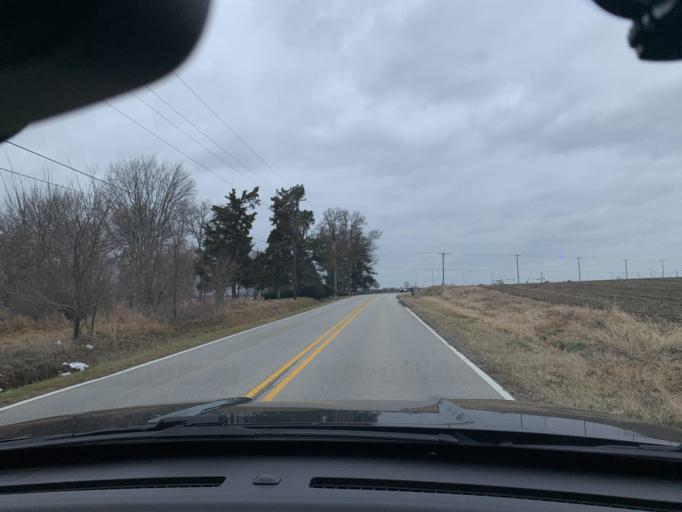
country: US
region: Illinois
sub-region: Sangamon County
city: Jerome
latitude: 39.7339
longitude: -89.6907
